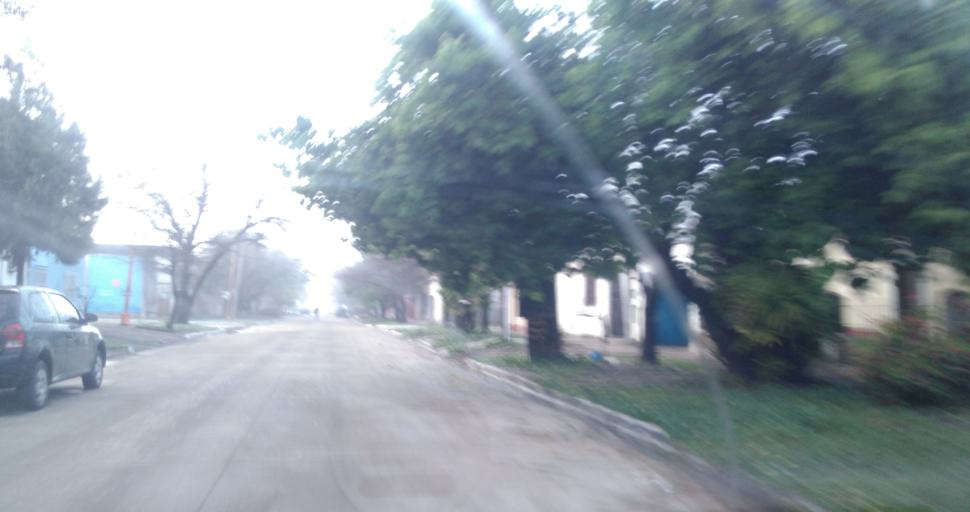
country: AR
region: Chaco
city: Resistencia
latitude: -27.4563
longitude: -58.9737
